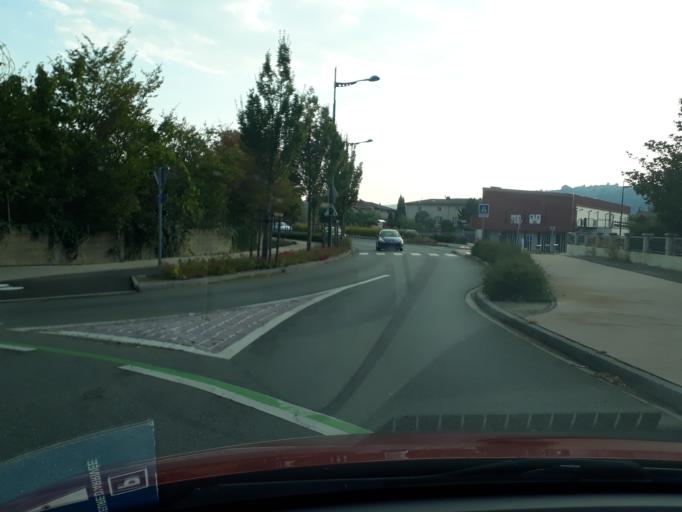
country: FR
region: Rhone-Alpes
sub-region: Departement du Rhone
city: Condrieu
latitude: 45.4600
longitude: 4.7689
